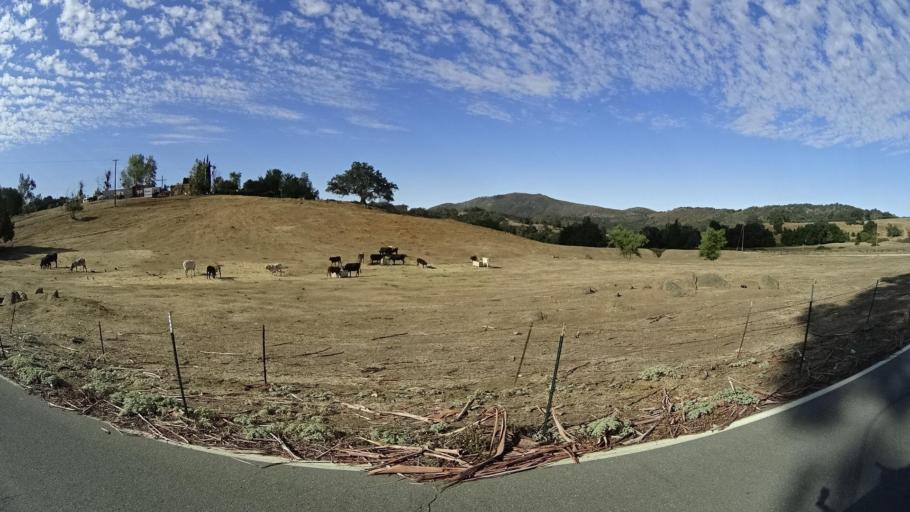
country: US
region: California
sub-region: San Diego County
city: Ramona
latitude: 33.1790
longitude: -116.7684
